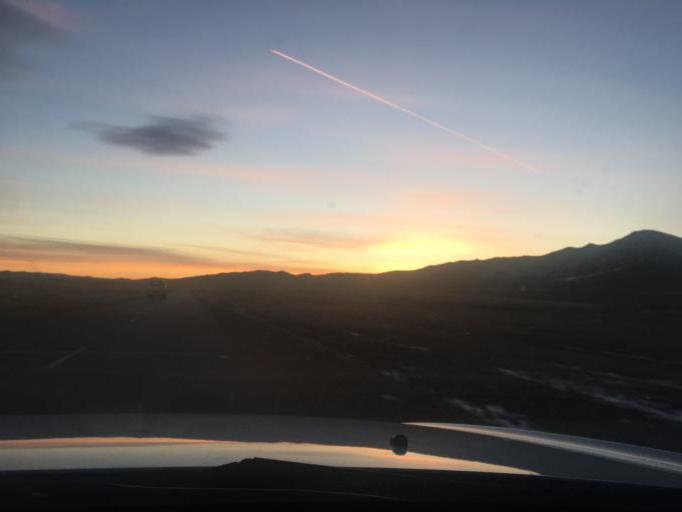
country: MN
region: Central Aimak
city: Mandal
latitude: 48.0892
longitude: 106.5994
